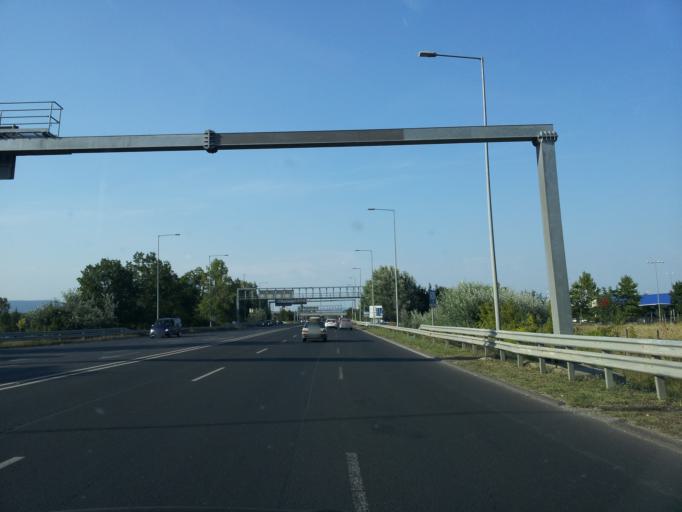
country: HU
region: Pest
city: Budakalasz
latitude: 47.6160
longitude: 19.0653
